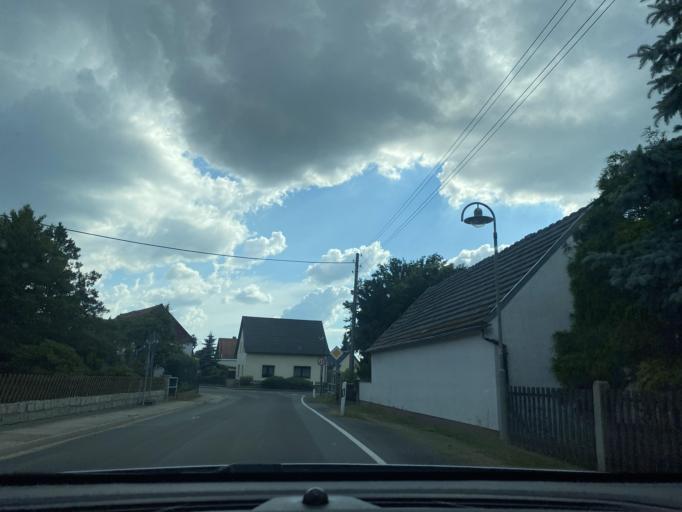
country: DE
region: Saxony
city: Klitten
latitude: 51.3505
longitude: 14.6033
